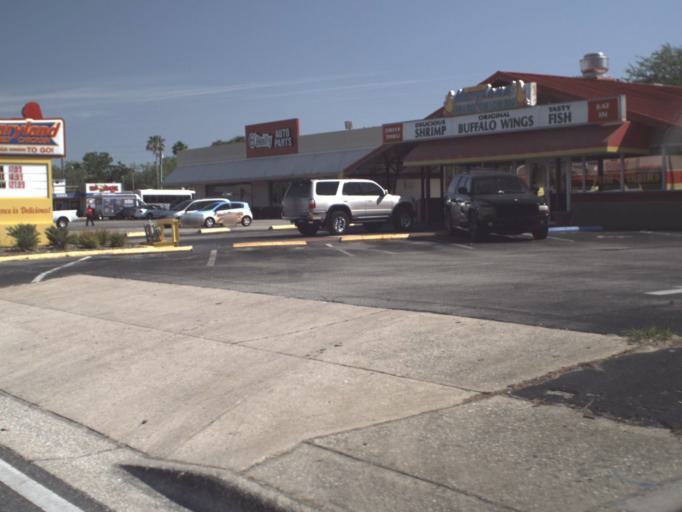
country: US
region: Florida
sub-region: Lake County
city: Leesburg
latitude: 28.8180
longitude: -81.8872
